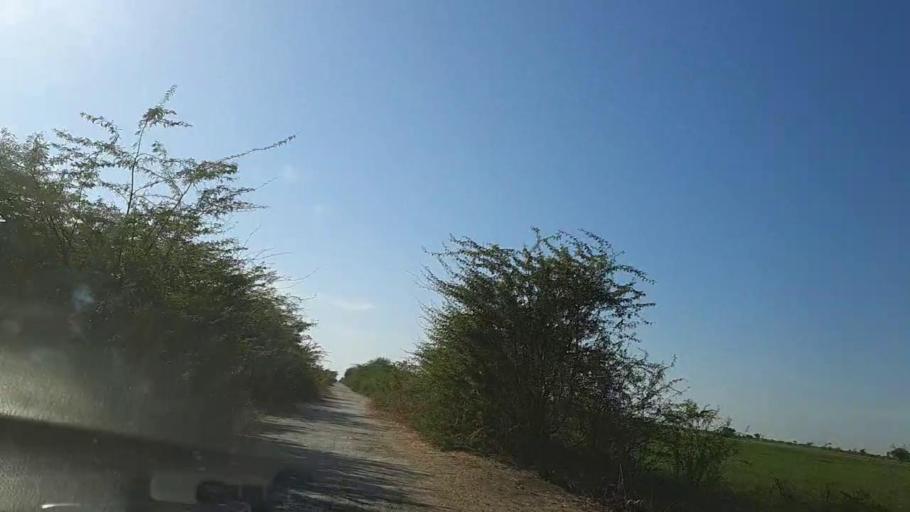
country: PK
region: Sindh
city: Dhoro Naro
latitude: 25.5054
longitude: 69.5154
